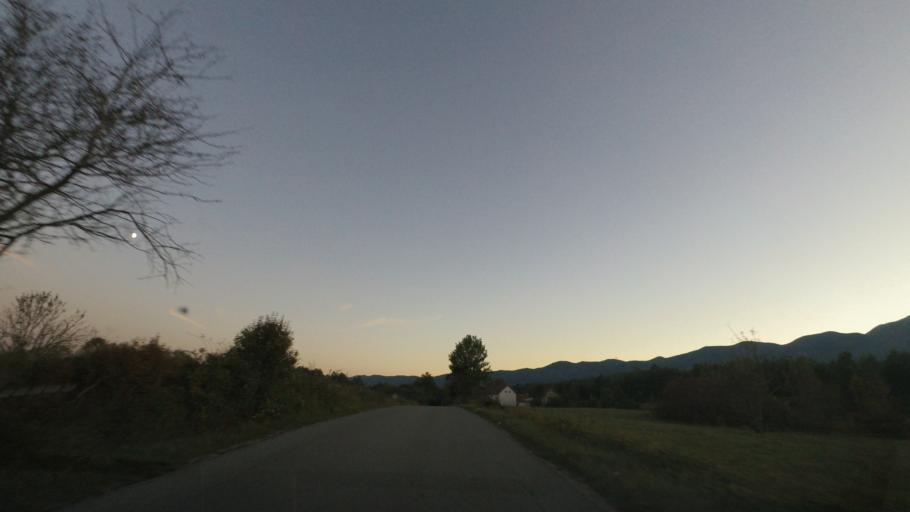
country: HR
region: Zadarska
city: Obrovac
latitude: 44.3749
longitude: 15.6462
